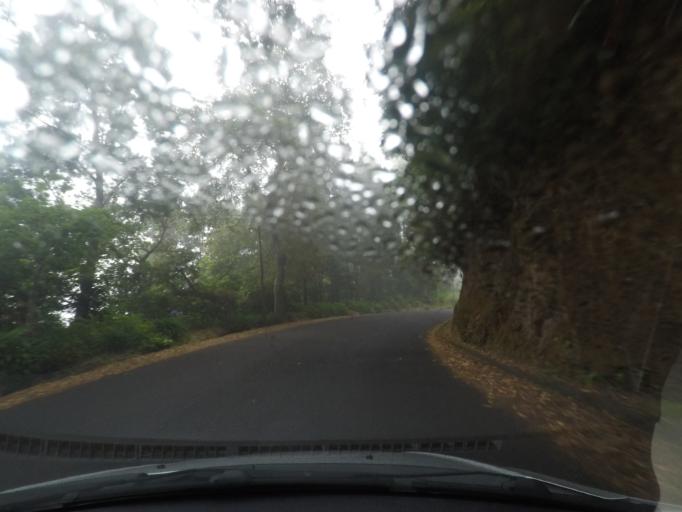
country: PT
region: Madeira
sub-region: Santana
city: Santana
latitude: 32.7492
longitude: -16.8716
